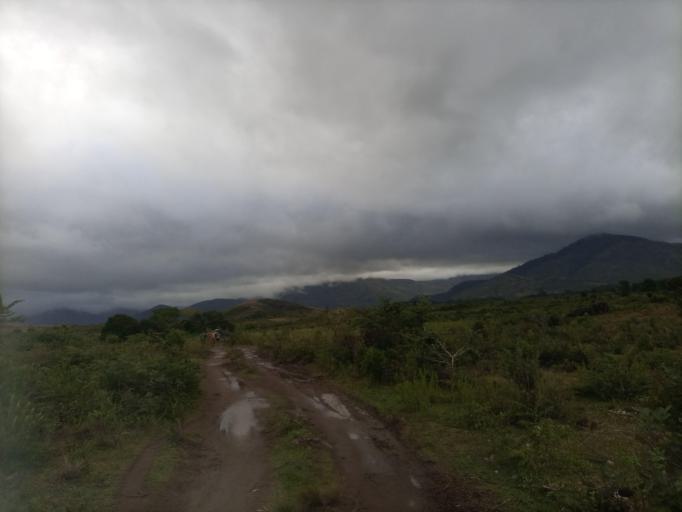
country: MG
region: Anosy
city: Fort Dauphin
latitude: -24.7603
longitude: 47.0705
